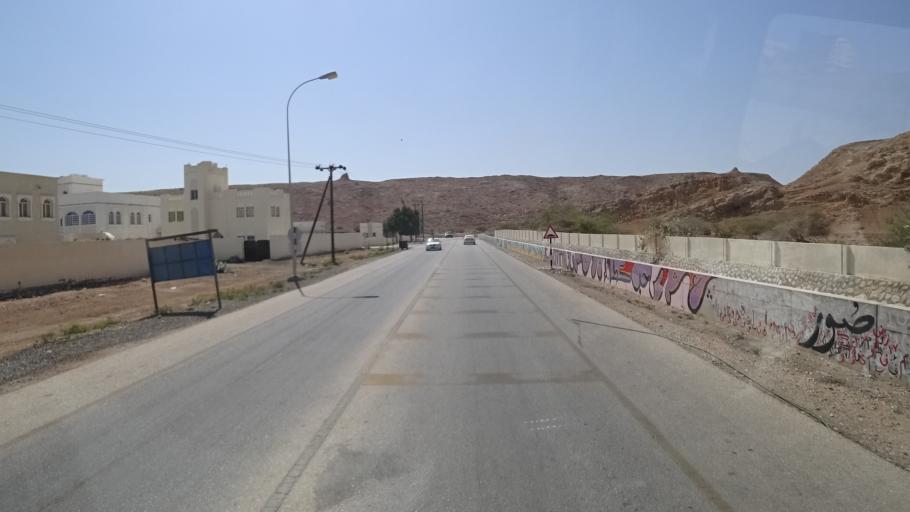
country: OM
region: Ash Sharqiyah
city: Sur
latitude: 22.5632
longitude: 59.5439
